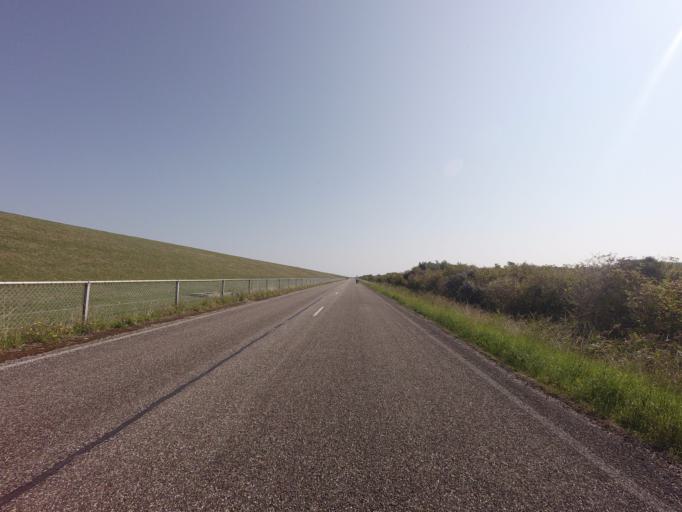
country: NL
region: Friesland
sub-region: Gemeente Schiermonnikoog
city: Schiermonnikoog
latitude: 53.4102
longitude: 6.2220
